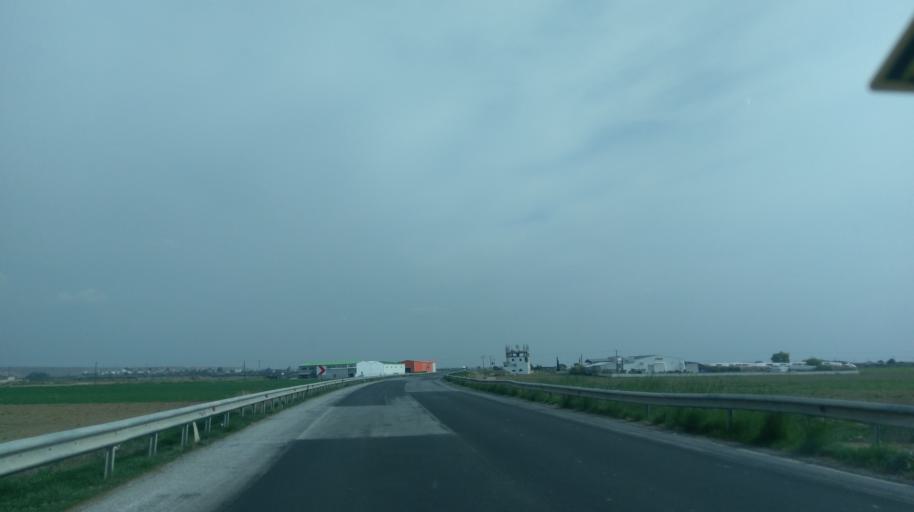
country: CY
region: Lefkosia
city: Geri
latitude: 35.2274
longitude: 33.5253
